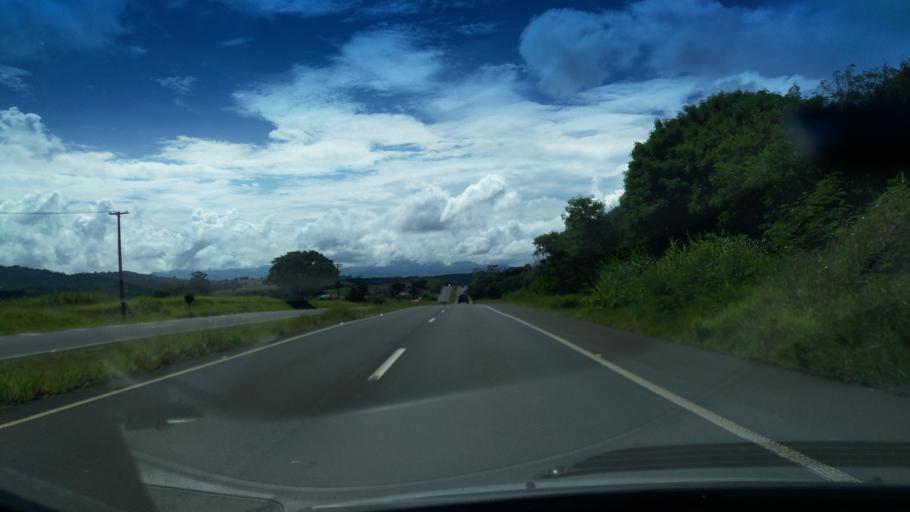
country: BR
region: Sao Paulo
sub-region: Santo Antonio Do Jardim
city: Espirito Santo do Pinhal
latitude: -22.1758
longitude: -46.7488
